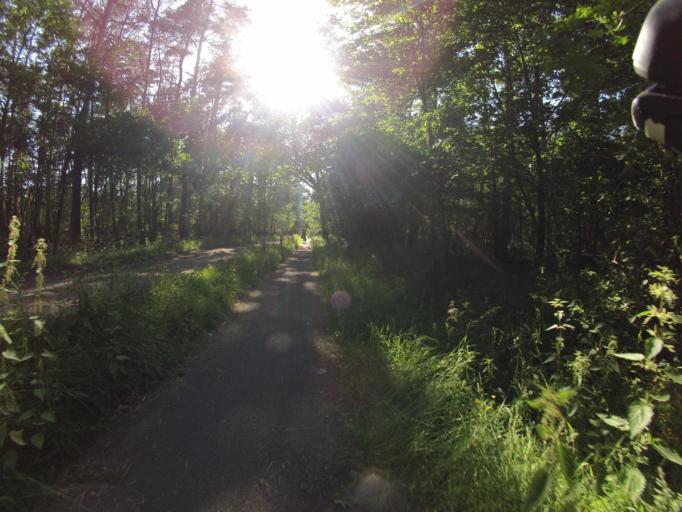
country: DE
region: Lower Saxony
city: Ohne
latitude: 52.3081
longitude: 7.2955
